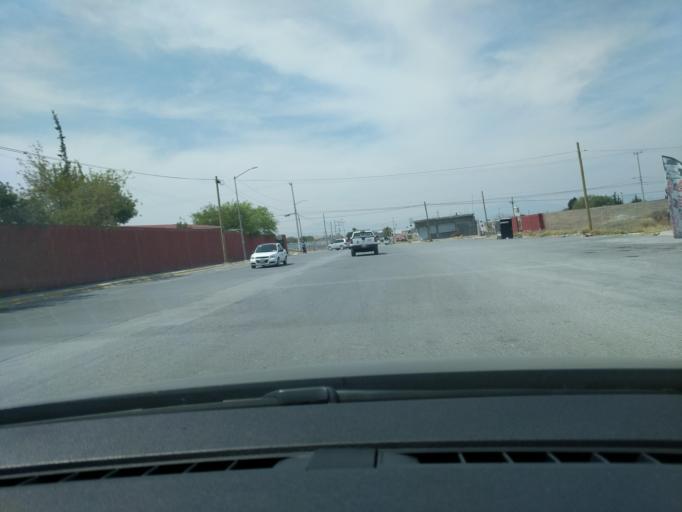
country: MX
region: Coahuila
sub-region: Arteaga
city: Arteaga
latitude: 25.4283
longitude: -100.9080
